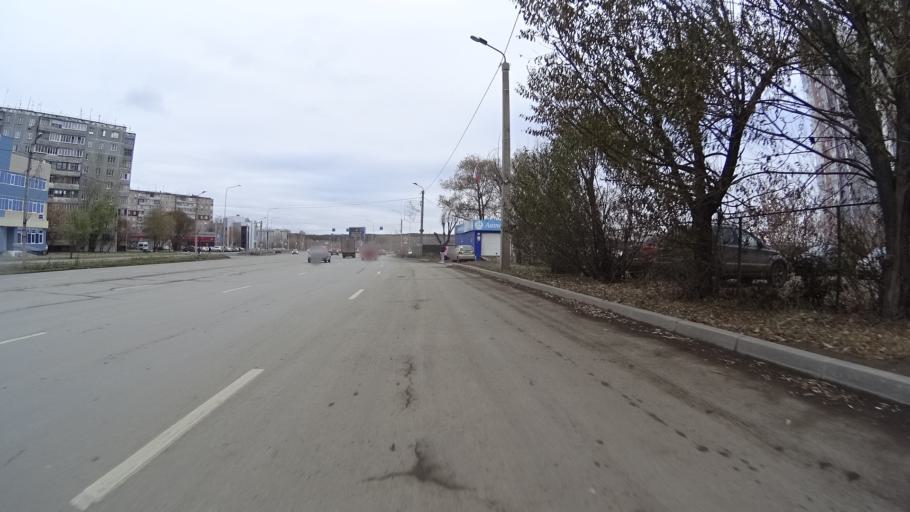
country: RU
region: Chelyabinsk
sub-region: Gorod Chelyabinsk
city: Chelyabinsk
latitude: 55.1763
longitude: 61.3332
